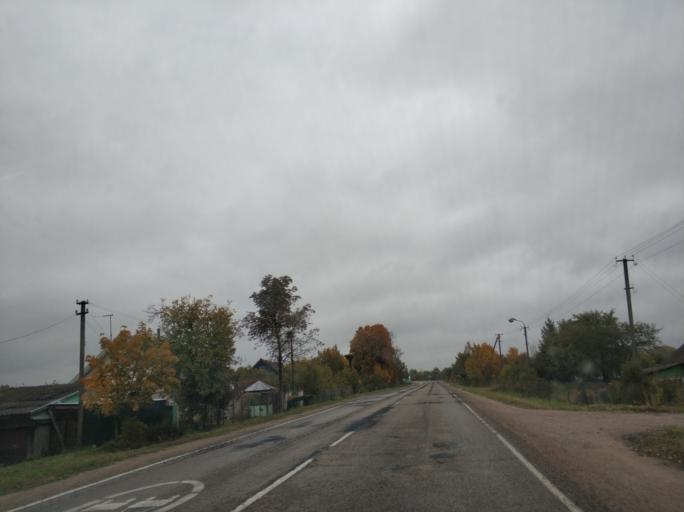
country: BY
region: Vitebsk
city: Rasony
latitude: 56.0535
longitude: 28.7110
